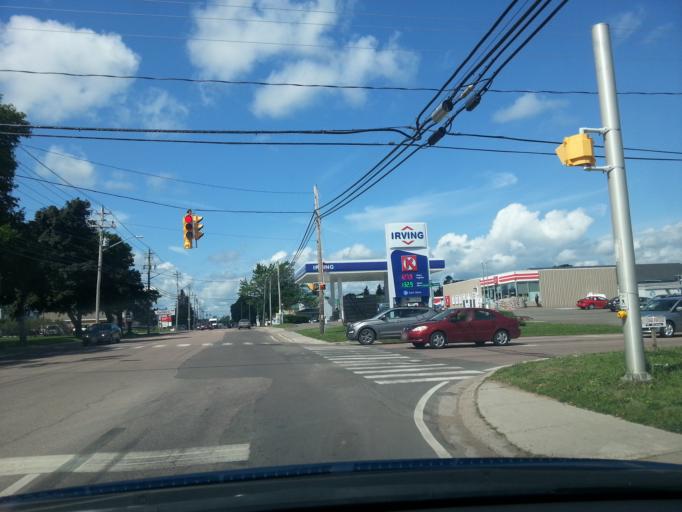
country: CA
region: New Brunswick
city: Shediac
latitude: 46.2246
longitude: -64.5131
